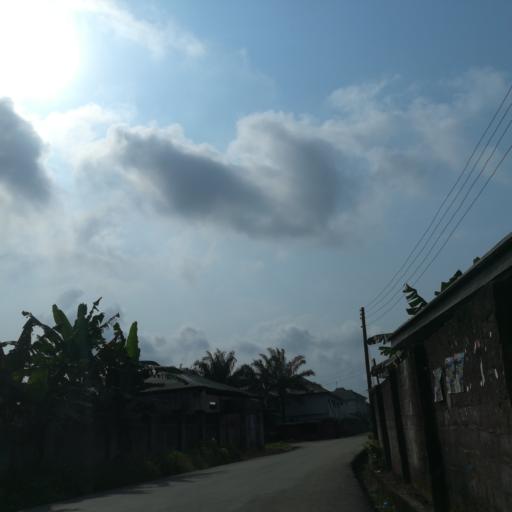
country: NG
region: Rivers
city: Okrika
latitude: 4.7800
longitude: 7.1366
